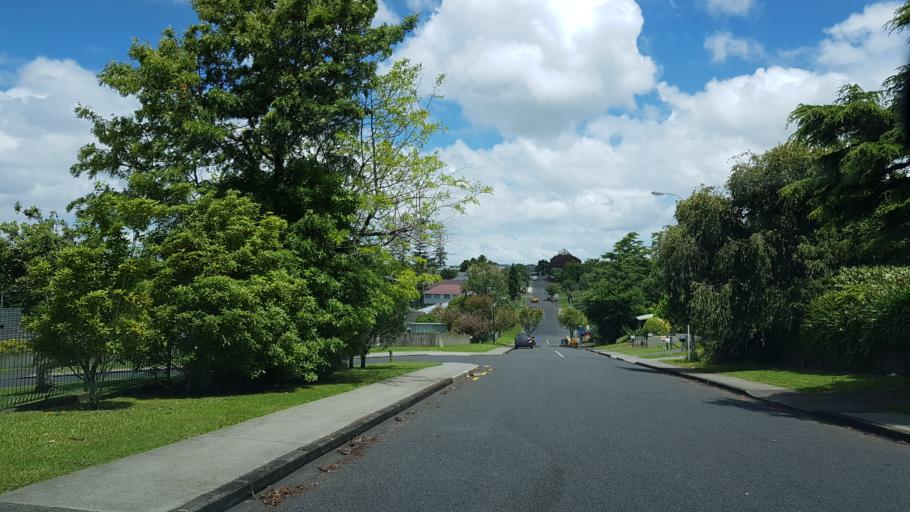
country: NZ
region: Auckland
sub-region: Auckland
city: North Shore
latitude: -36.7993
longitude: 174.7419
